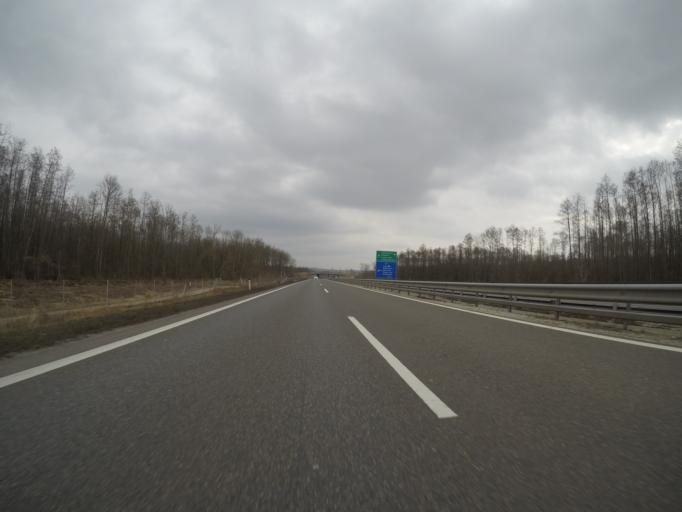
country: SI
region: Lendava-Lendva
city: Lendava
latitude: 46.5953
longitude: 16.4153
